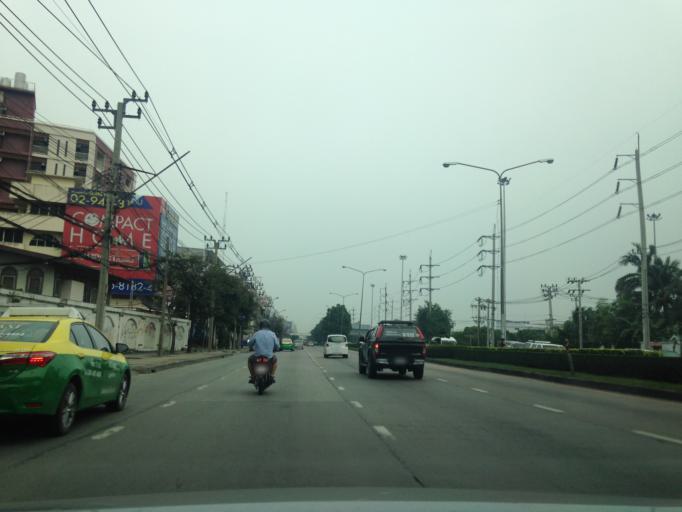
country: TH
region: Bangkok
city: Bang Khen
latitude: 13.8492
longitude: 100.6431
